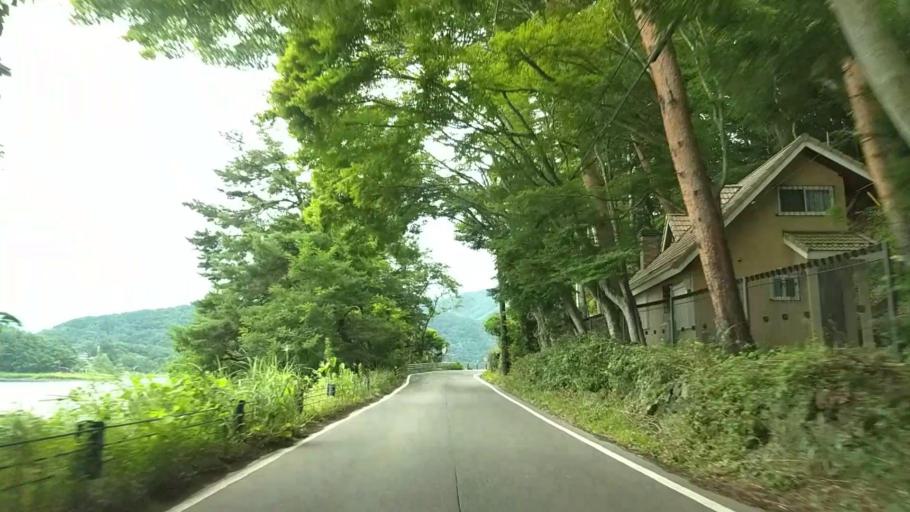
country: JP
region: Yamanashi
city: Fujikawaguchiko
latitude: 35.5135
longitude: 138.7348
